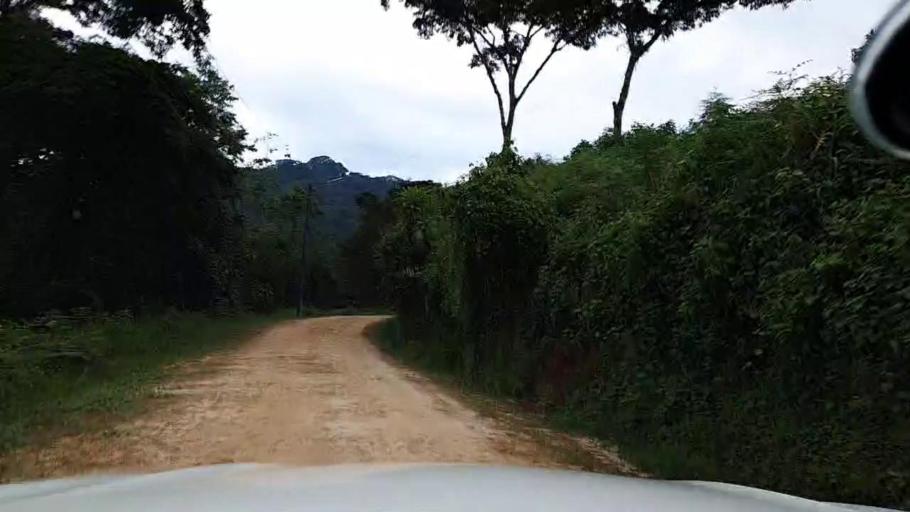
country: RW
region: Western Province
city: Cyangugu
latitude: -2.5683
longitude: 29.2289
